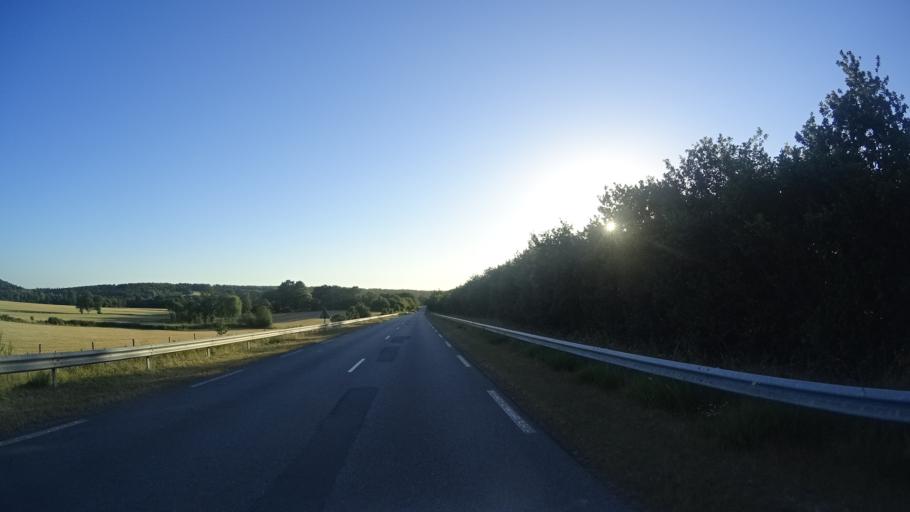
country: FR
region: Brittany
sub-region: Departement d'Ille-et-Vilaine
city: Langon
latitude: 47.7189
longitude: -1.8982
